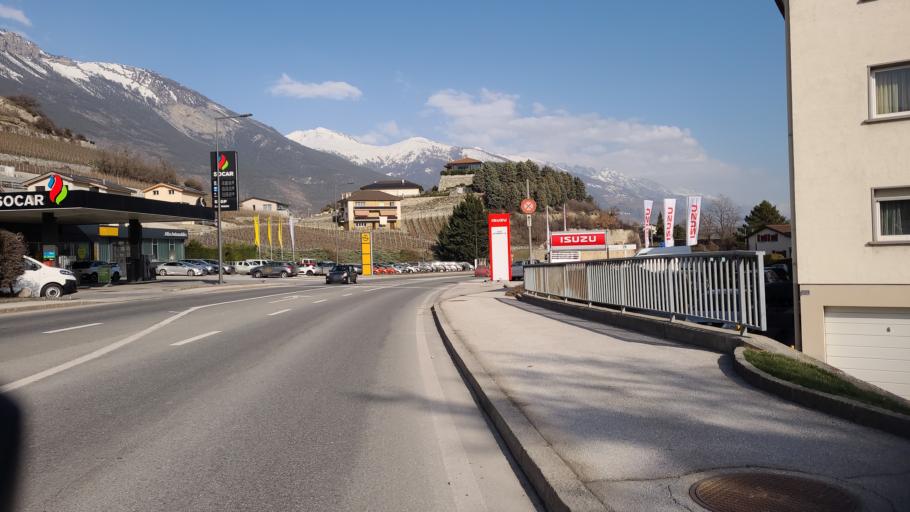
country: CH
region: Valais
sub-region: Sierre District
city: Veyras
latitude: 46.2981
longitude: 7.5463
